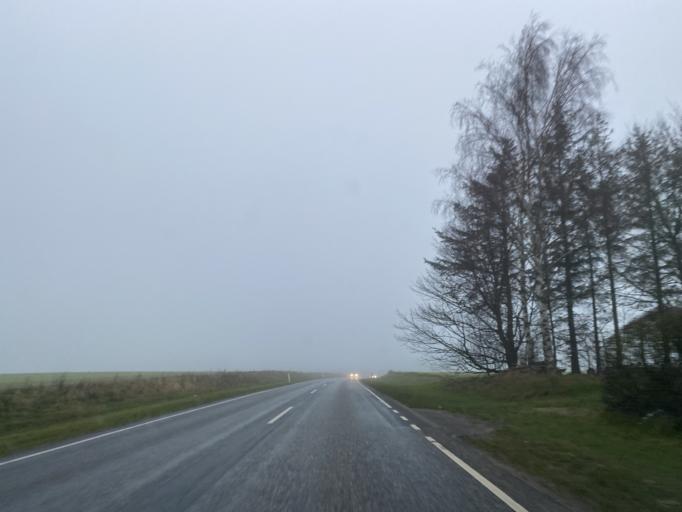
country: DK
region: Central Jutland
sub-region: Arhus Kommune
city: Solbjerg
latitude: 55.9860
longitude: 10.0347
